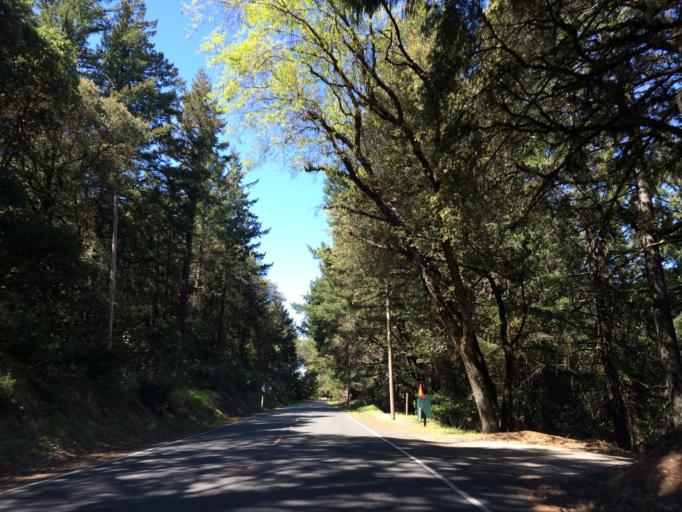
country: US
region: California
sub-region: Santa Clara County
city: Saratoga
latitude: 37.2427
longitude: -122.1076
